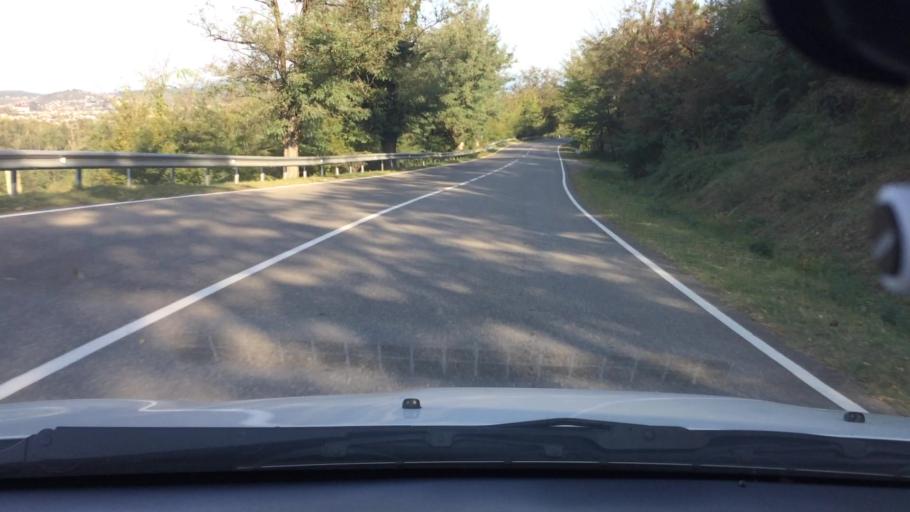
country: GE
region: Imereti
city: Kutaisi
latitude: 42.2524
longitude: 42.7499
